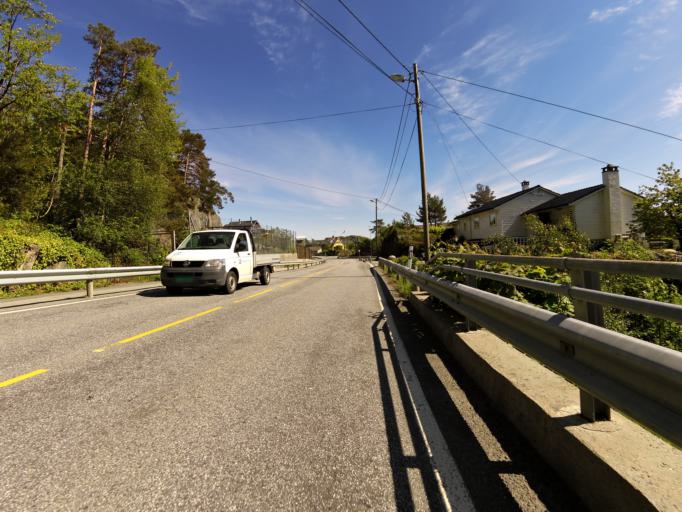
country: NO
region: Hordaland
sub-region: Stord
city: Sagvag
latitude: 59.7804
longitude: 5.3906
